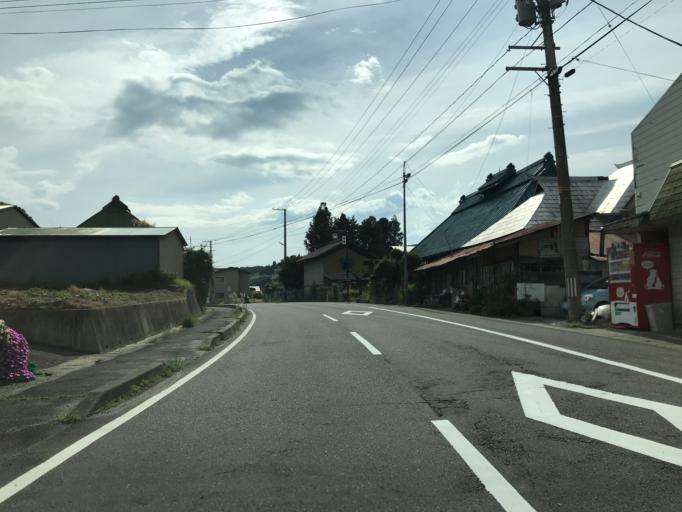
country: JP
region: Fukushima
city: Funehikimachi-funehiki
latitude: 37.5040
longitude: 140.6032
